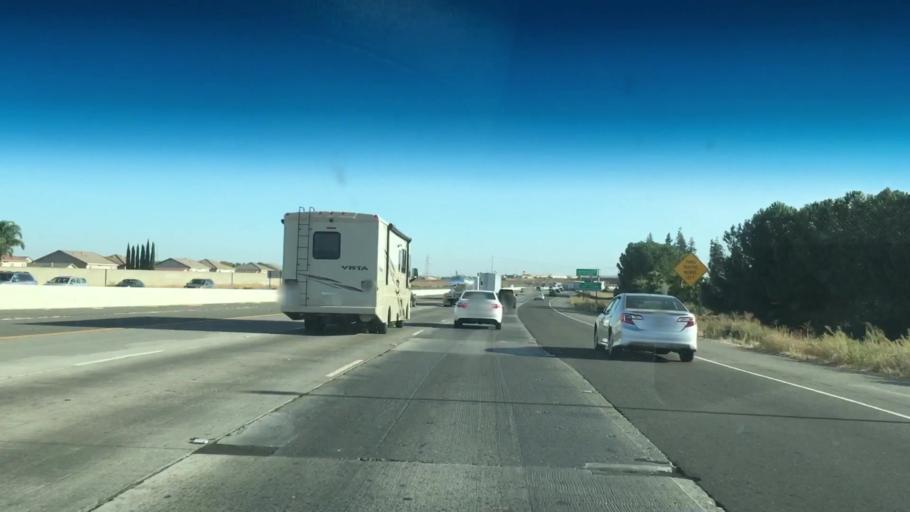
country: US
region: California
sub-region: Sacramento County
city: Parkway
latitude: 38.4731
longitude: -121.5017
